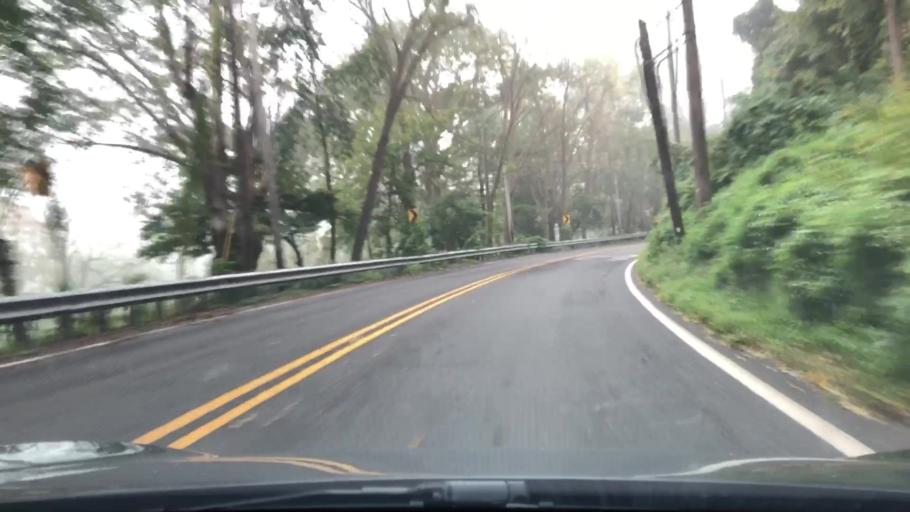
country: US
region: Pennsylvania
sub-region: Delaware County
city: Radnor
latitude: 40.0256
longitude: -75.3659
